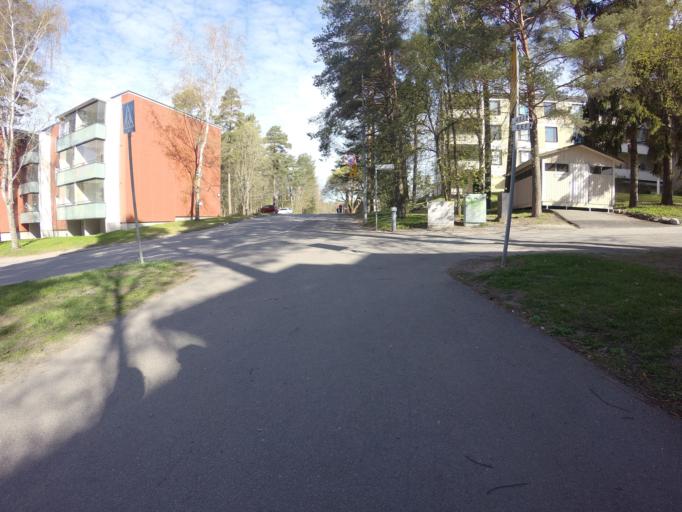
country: FI
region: Varsinais-Suomi
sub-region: Turku
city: Raisio
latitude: 60.4562
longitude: 22.1616
